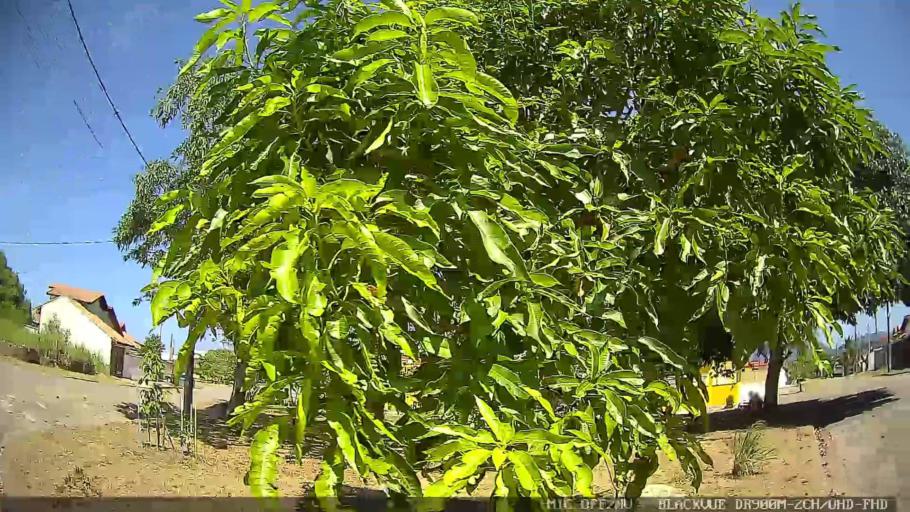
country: BR
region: Sao Paulo
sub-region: Peruibe
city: Peruibe
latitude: -24.2971
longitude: -46.9786
